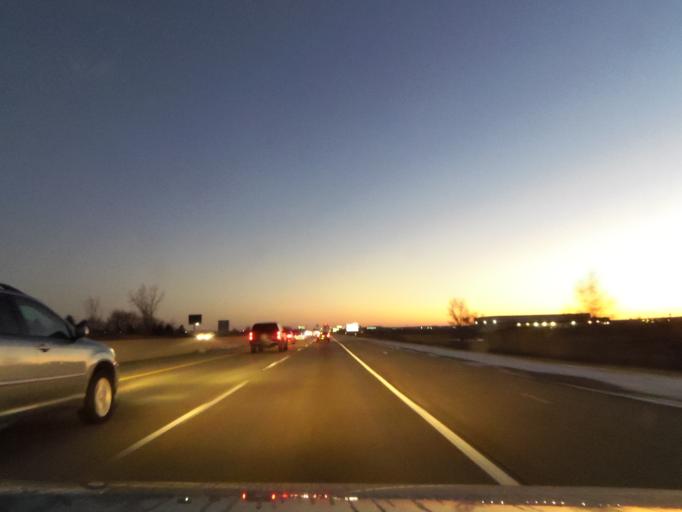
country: US
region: Indiana
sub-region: Lake County
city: Merrillville
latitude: 41.4475
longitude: -87.3217
